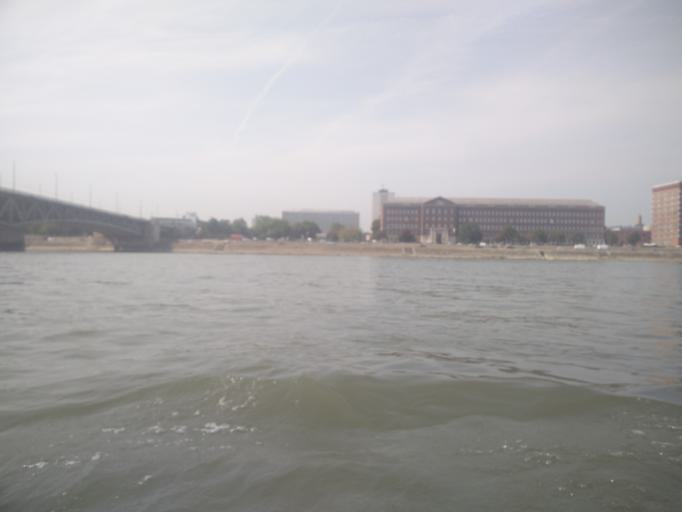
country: HU
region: Budapest
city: Budapest IX. keruelet
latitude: 47.4803
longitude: 19.0637
